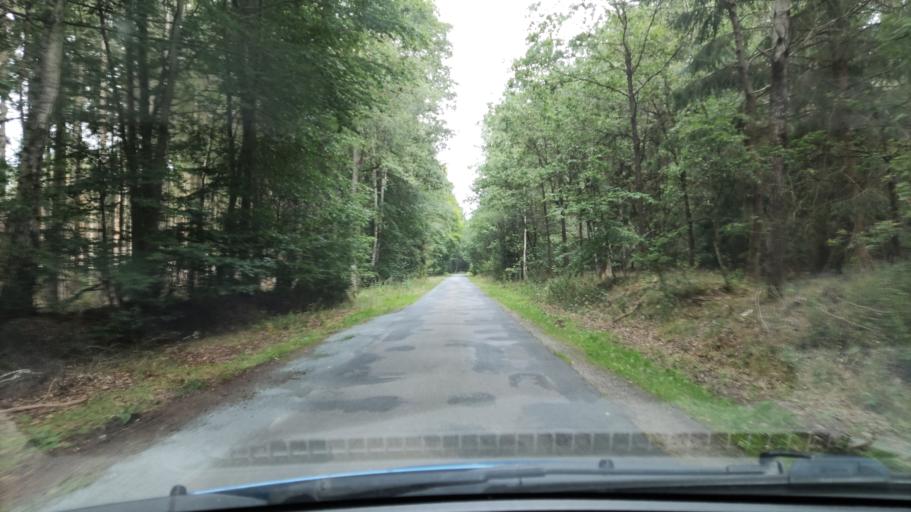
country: DE
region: Lower Saxony
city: Schnega
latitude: 52.9255
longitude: 10.8804
